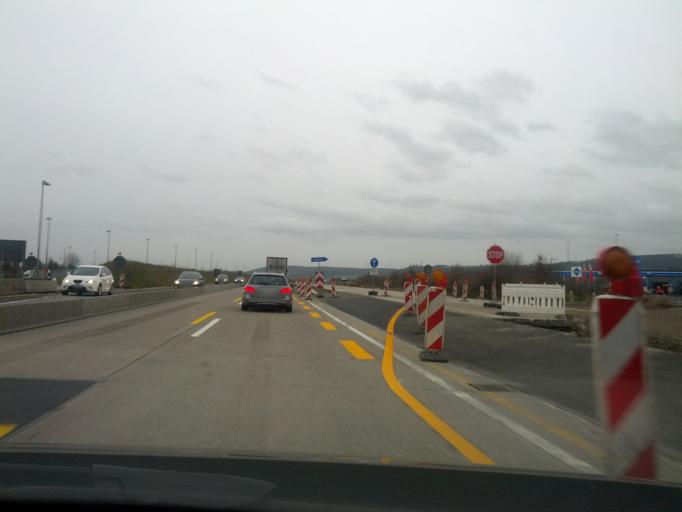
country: DE
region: Lower Saxony
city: Seesen
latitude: 51.9299
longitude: 10.1441
